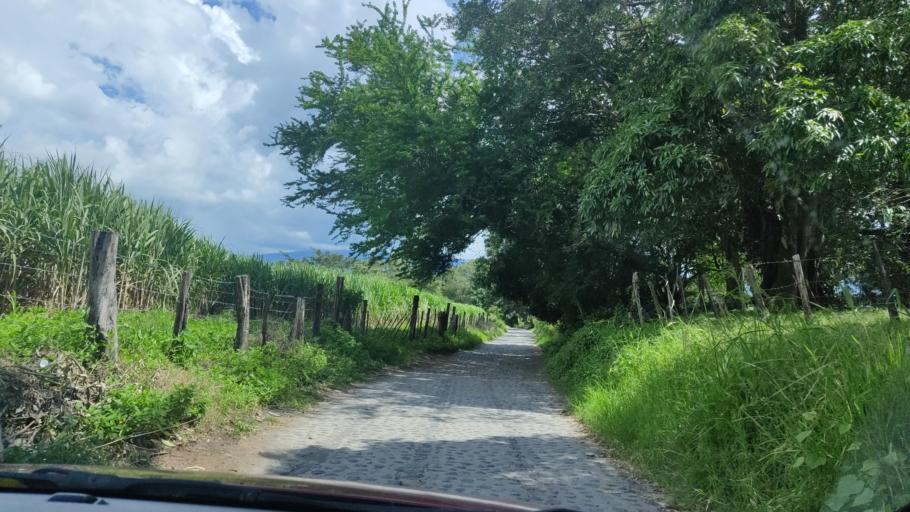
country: MX
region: Nayarit
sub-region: Ahuacatlan
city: Ahuacatlan
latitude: 21.1178
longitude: -104.6191
